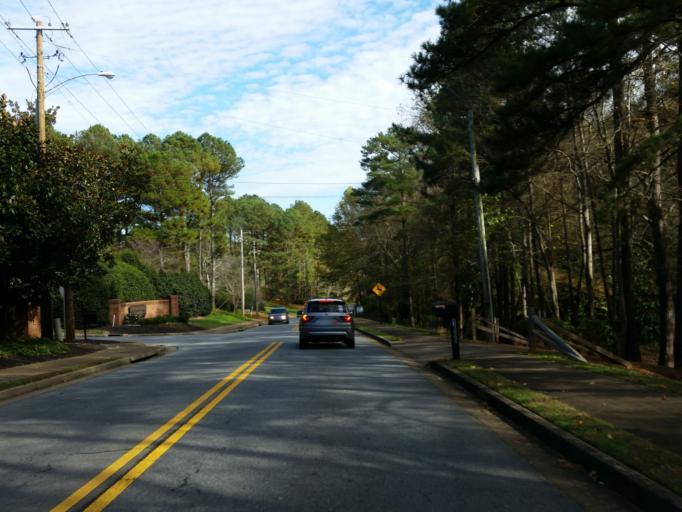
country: US
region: Georgia
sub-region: Cherokee County
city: Woodstock
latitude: 34.0405
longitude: -84.5022
